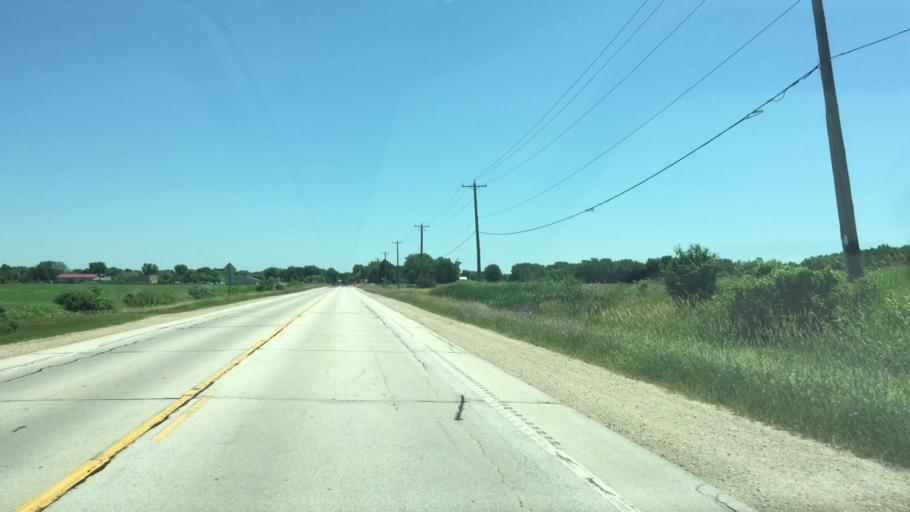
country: US
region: Wisconsin
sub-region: Calumet County
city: Hilbert
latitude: 44.1401
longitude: -88.1816
